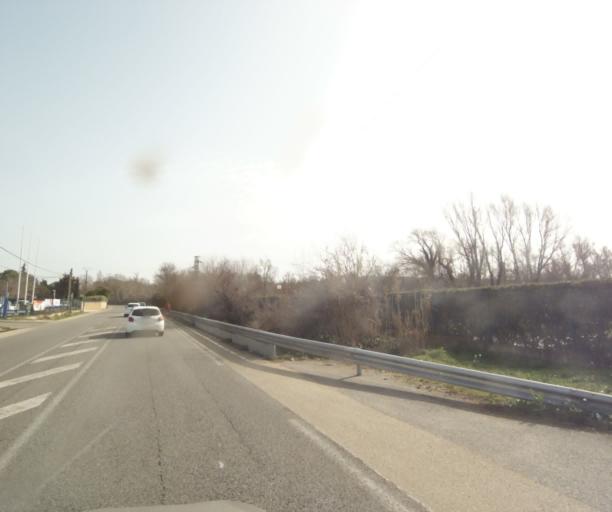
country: FR
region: Provence-Alpes-Cote d'Azur
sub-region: Departement des Bouches-du-Rhone
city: Aix-en-Provence
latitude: 43.5105
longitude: 5.4148
